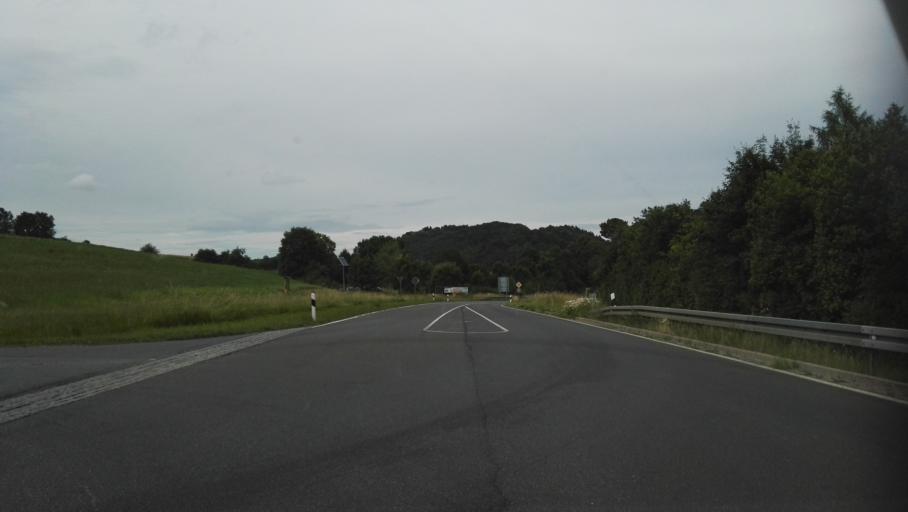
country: DE
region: Bavaria
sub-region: Upper Franconia
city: Plankenfels
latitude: 49.8817
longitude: 11.3383
